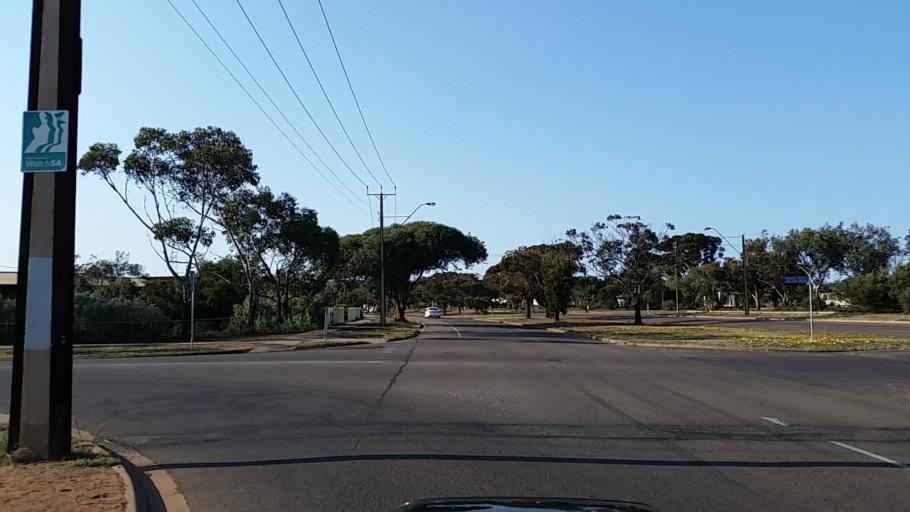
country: AU
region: South Australia
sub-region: Whyalla
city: Whyalla
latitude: -33.0239
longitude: 137.5313
